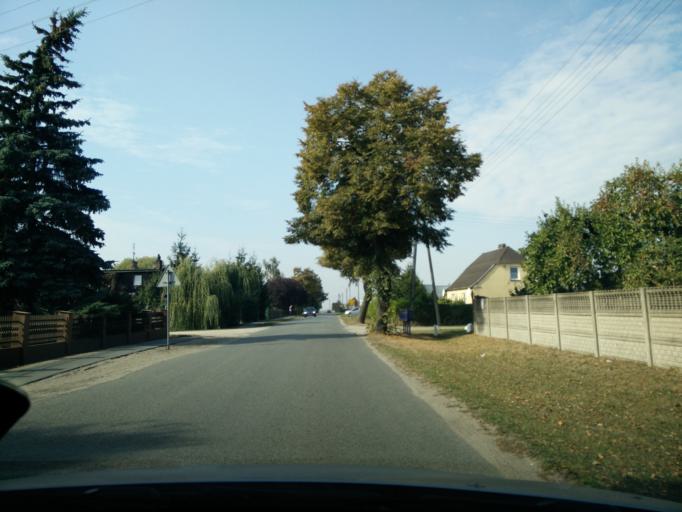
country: PL
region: Greater Poland Voivodeship
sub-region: Powiat sredzki
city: Sroda Wielkopolska
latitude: 52.3051
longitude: 17.2780
